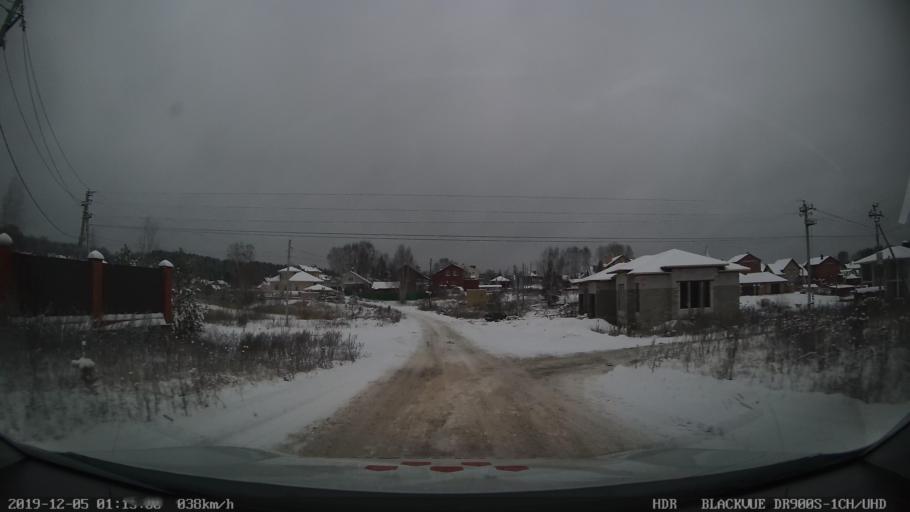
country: RU
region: Tatarstan
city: Stolbishchi
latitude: 55.6446
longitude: 49.1141
